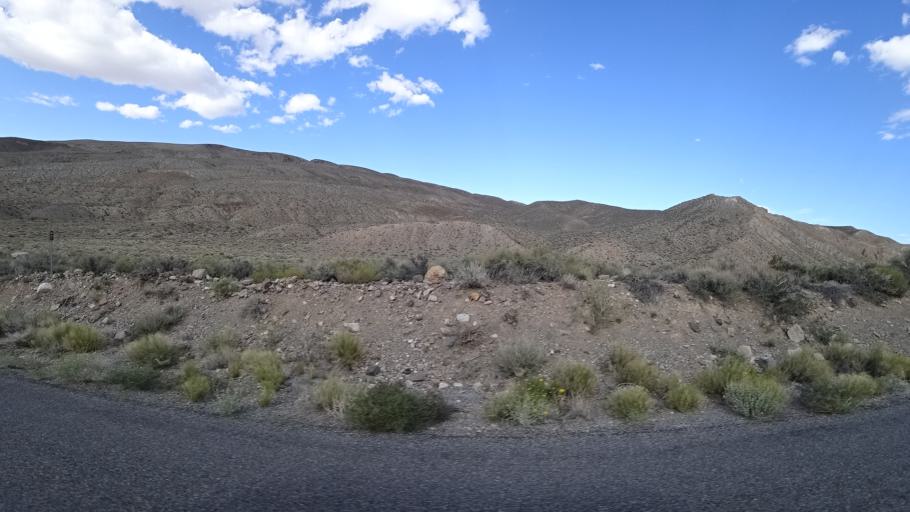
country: US
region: Nevada
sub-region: Nye County
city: Beatty
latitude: 36.4124
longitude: -117.1771
